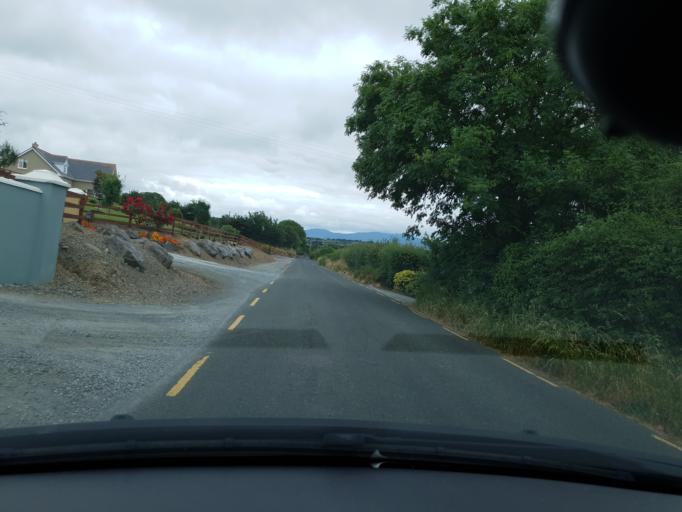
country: IE
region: Munster
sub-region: Ciarrai
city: Cill Airne
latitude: 52.1364
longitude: -9.5831
